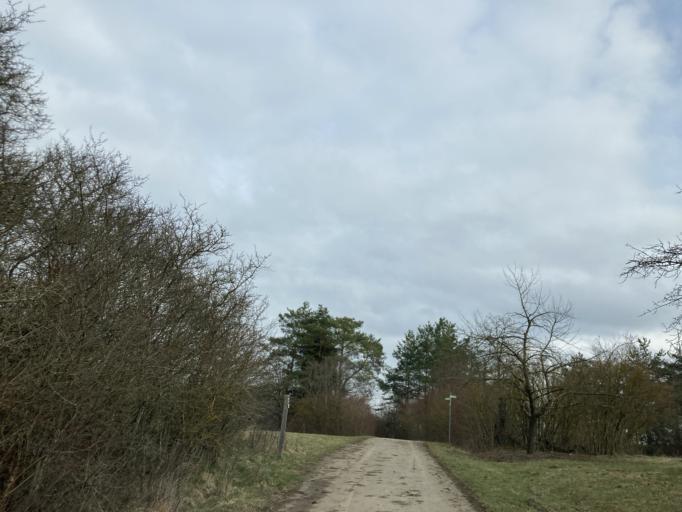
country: DE
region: Baden-Wuerttemberg
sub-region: Tuebingen Region
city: Rottenburg
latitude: 48.4474
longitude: 8.9122
